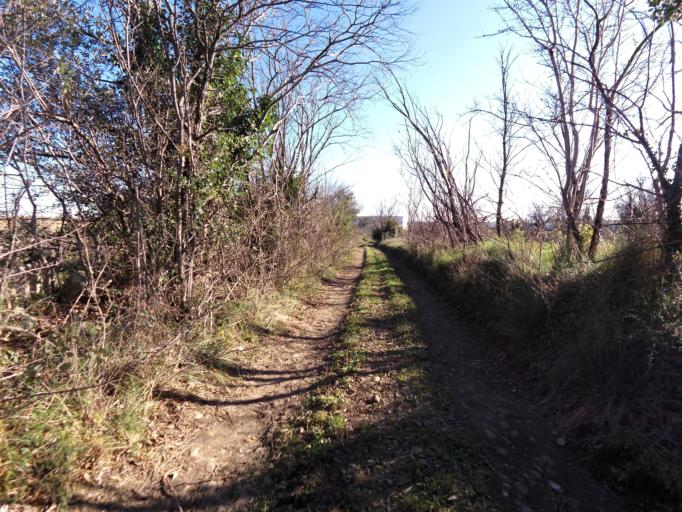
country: FR
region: Languedoc-Roussillon
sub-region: Departement du Gard
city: Mus
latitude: 43.7316
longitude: 4.1930
